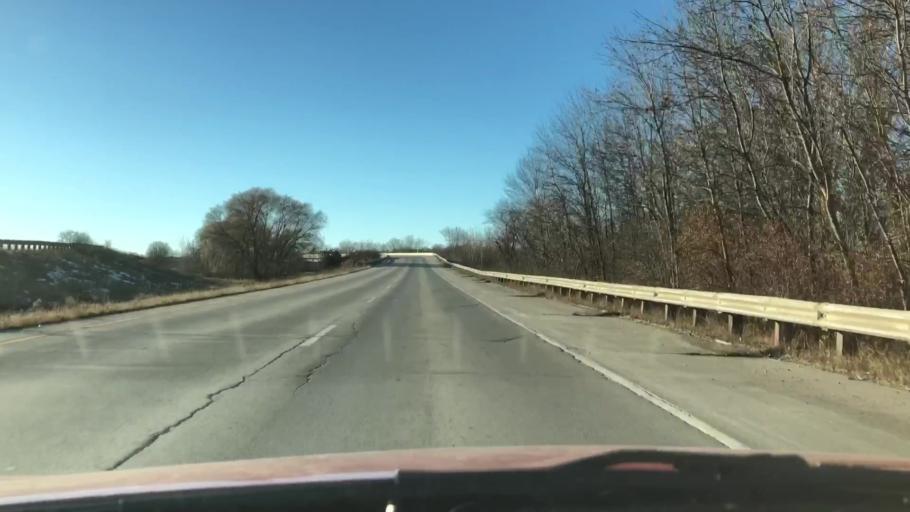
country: US
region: Wisconsin
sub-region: Brown County
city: De Pere
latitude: 44.4563
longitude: -88.0838
